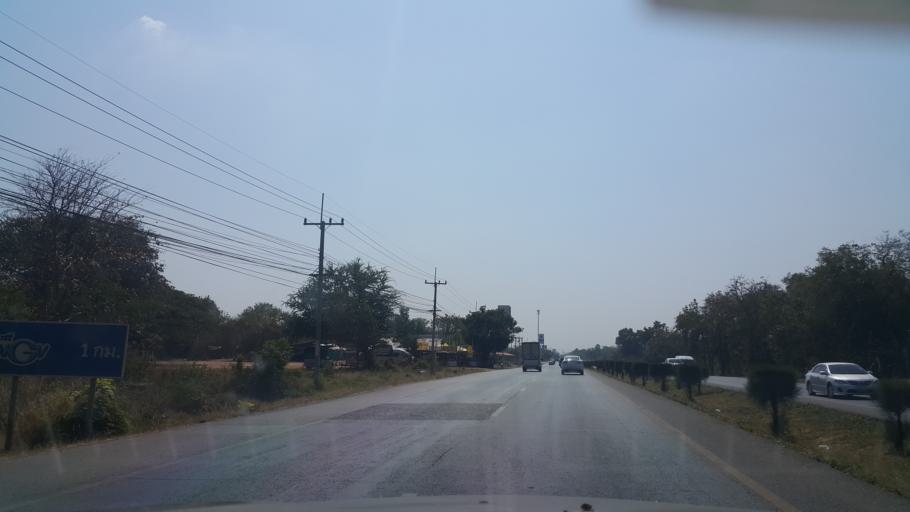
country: TH
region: Khon Kaen
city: Ban Phai
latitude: 16.0293
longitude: 102.7107
